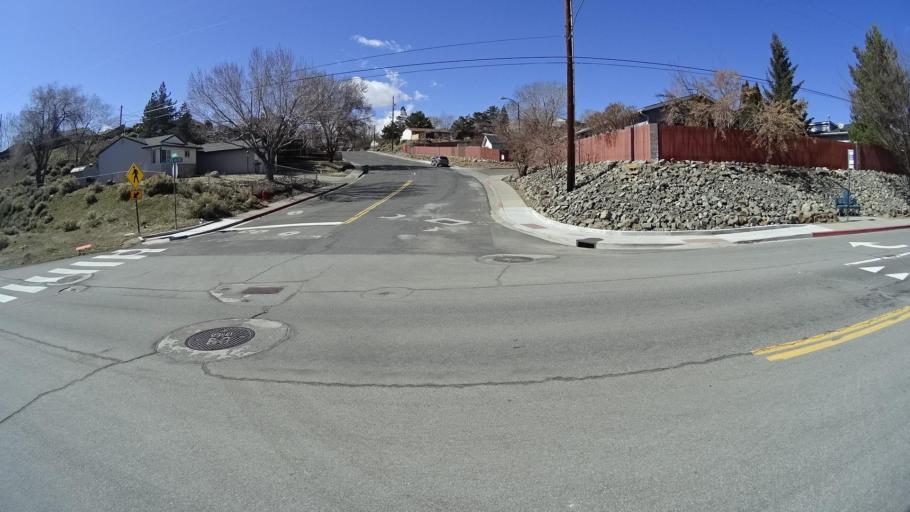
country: US
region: Nevada
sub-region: Washoe County
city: Golden Valley
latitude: 39.5902
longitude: -119.8352
